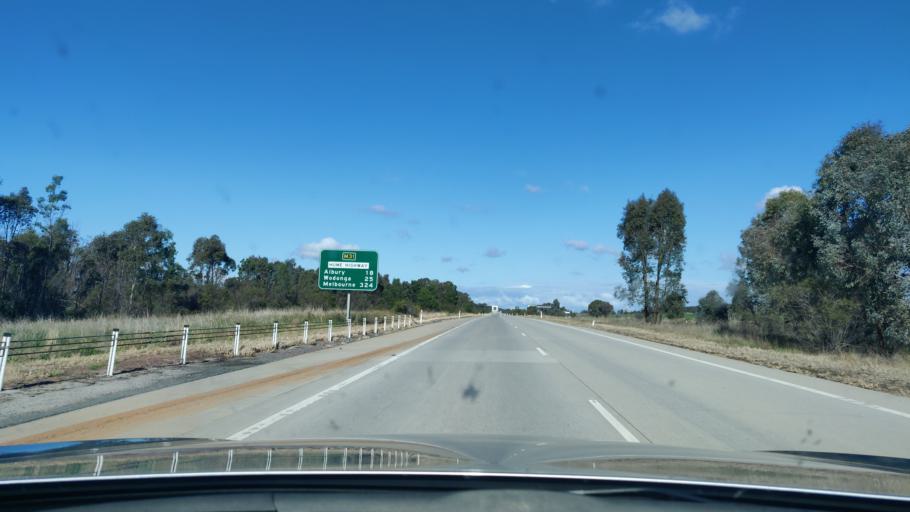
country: AU
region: New South Wales
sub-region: Greater Hume Shire
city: Jindera
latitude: -35.9410
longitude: 147.0035
